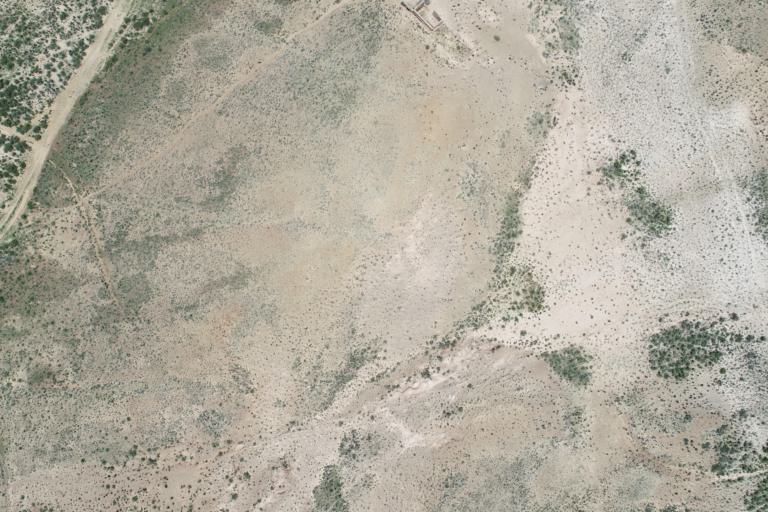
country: BO
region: La Paz
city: Curahuara de Carangas
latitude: -17.3073
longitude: -68.5065
